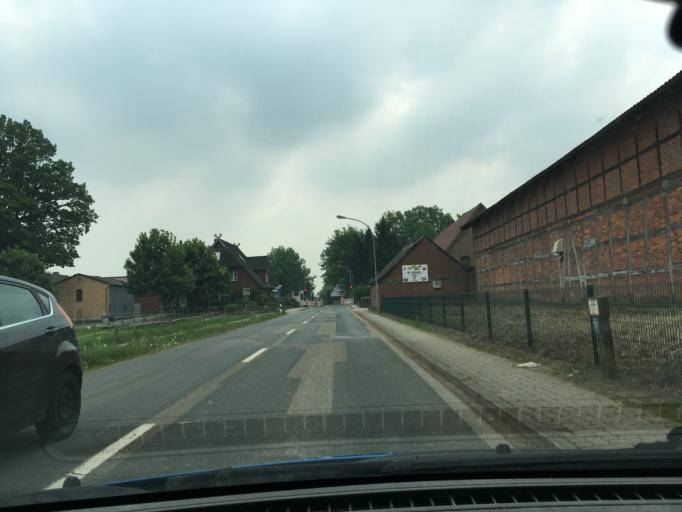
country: DE
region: Lower Saxony
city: Seevetal
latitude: 53.4231
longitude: 9.8978
